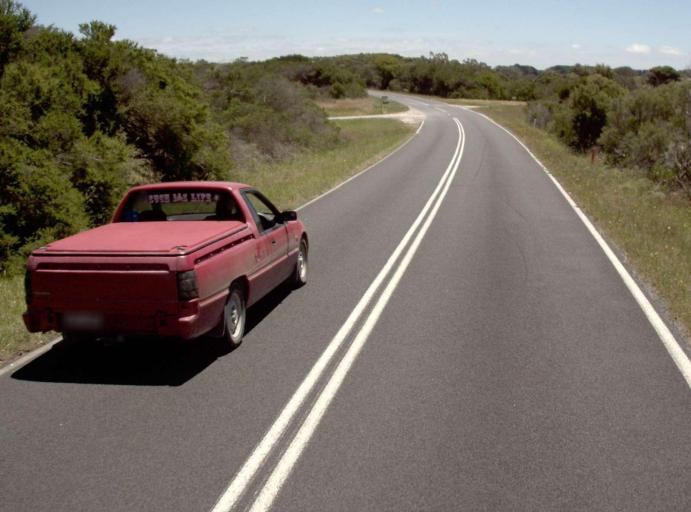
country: AU
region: Victoria
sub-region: Latrobe
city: Morwell
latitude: -38.8501
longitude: 146.2452
